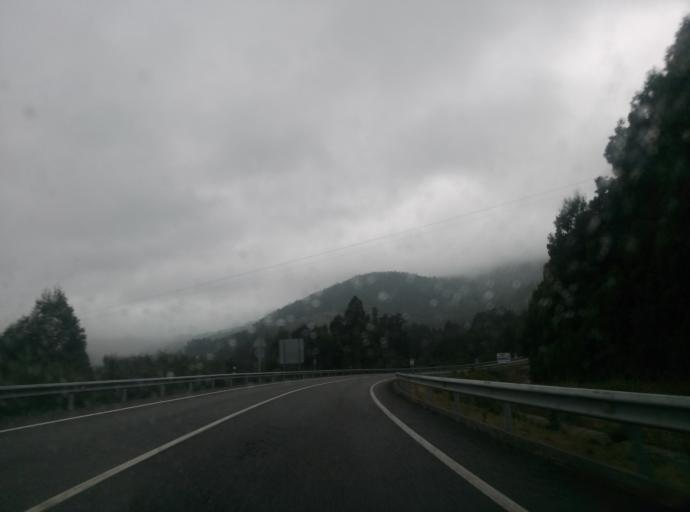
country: ES
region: Galicia
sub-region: Provincia de Lugo
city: Viveiro
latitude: 43.5736
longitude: -7.6341
